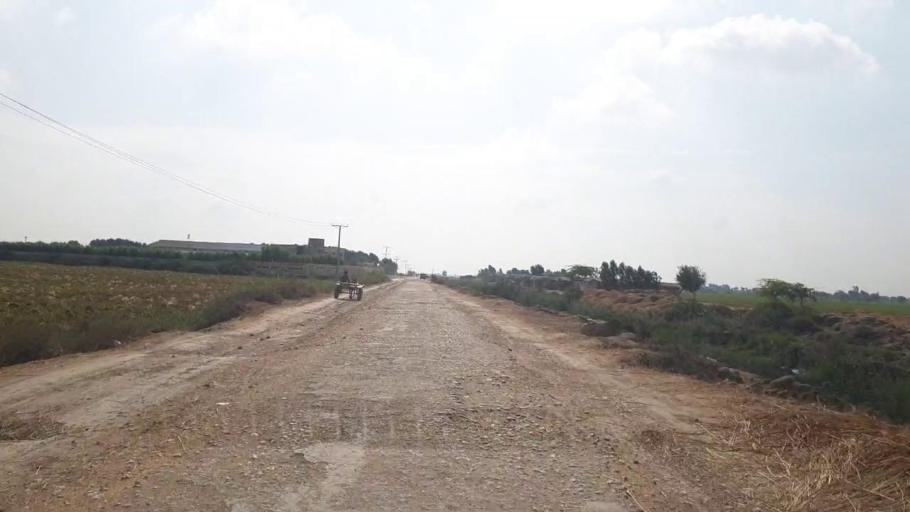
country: PK
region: Sindh
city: Kario
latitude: 24.6384
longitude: 68.5467
